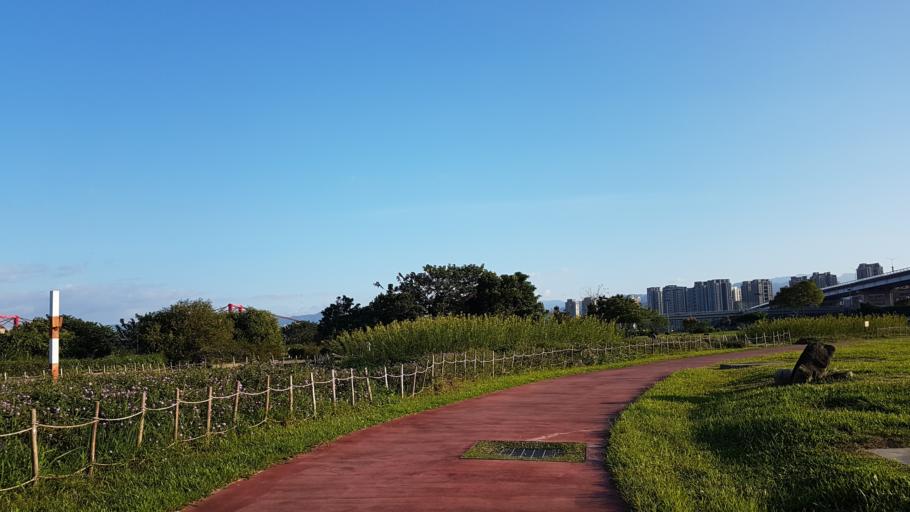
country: TW
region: Taipei
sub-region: Taipei
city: Banqiao
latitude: 25.0263
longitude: 121.4858
